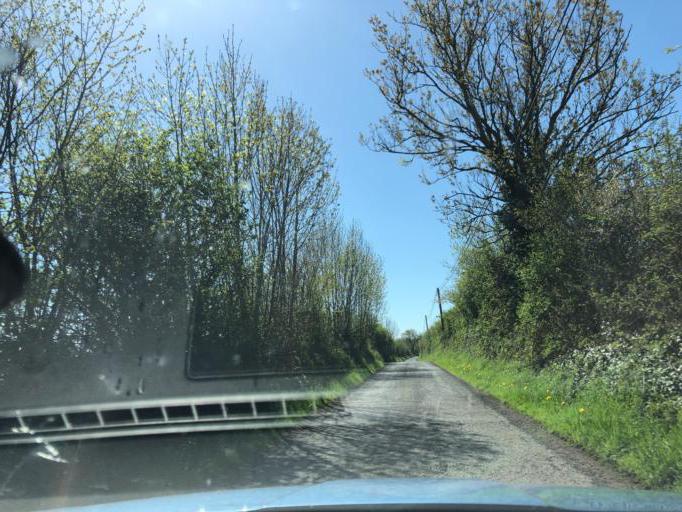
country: IE
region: Connaught
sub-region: County Galway
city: Portumna
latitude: 53.1321
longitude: -8.3333
